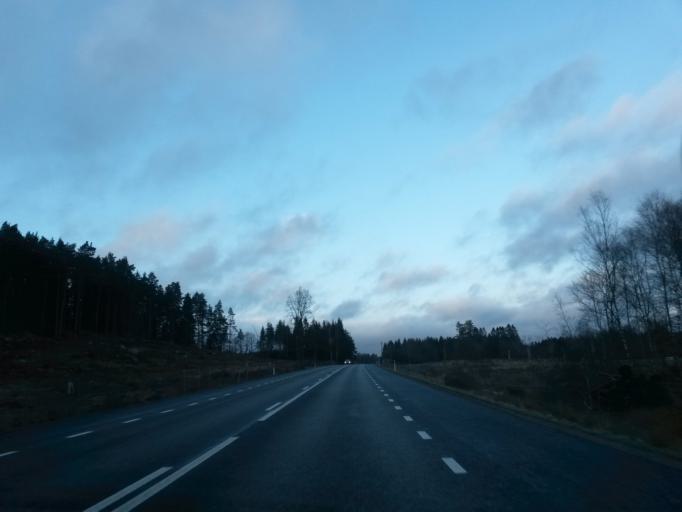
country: SE
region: Halland
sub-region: Halmstads Kommun
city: Aled
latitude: 56.7733
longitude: 12.9509
